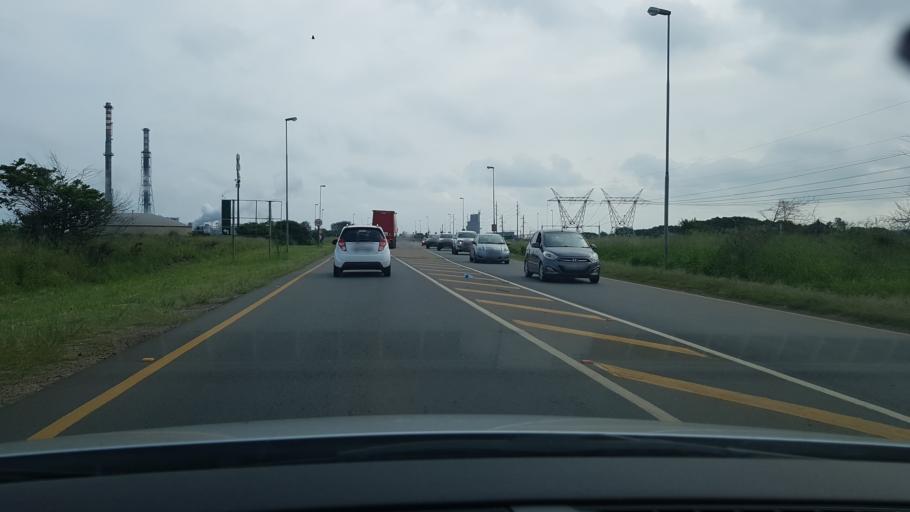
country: ZA
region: KwaZulu-Natal
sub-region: uThungulu District Municipality
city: Richards Bay
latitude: -28.7667
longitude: 32.0366
